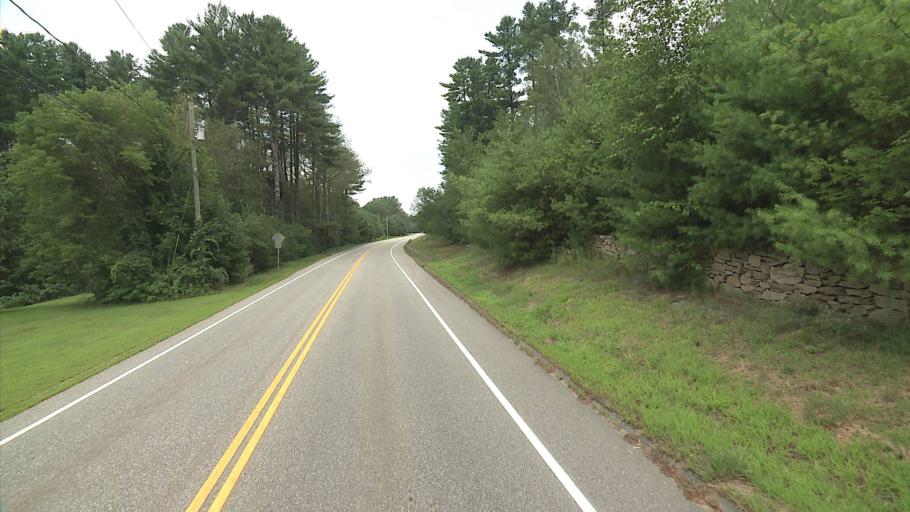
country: US
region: Connecticut
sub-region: Windham County
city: Wauregan
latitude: 41.7690
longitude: -71.9386
